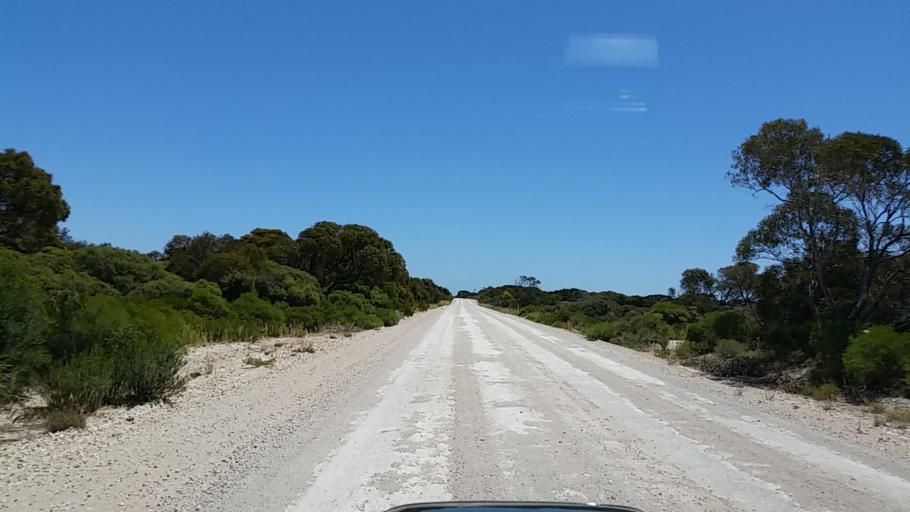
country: AU
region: South Australia
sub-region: Yorke Peninsula
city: Honiton
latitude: -35.2161
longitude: 137.0085
